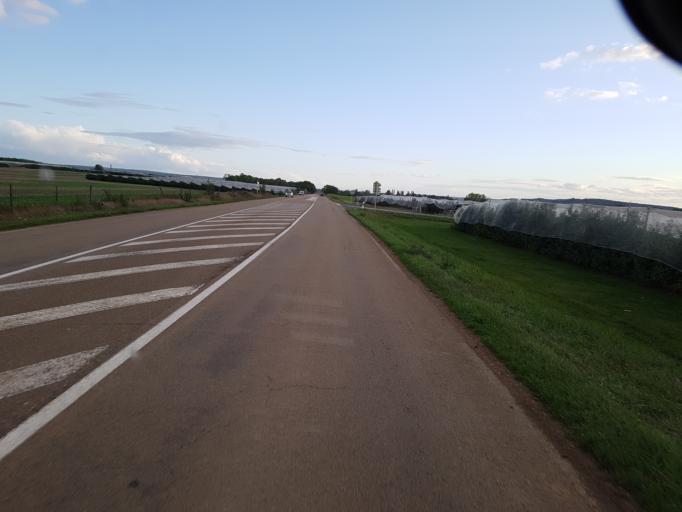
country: FR
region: Bourgogne
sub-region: Departement de l'Yonne
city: Saint-Clement
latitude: 48.2489
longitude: 3.2850
